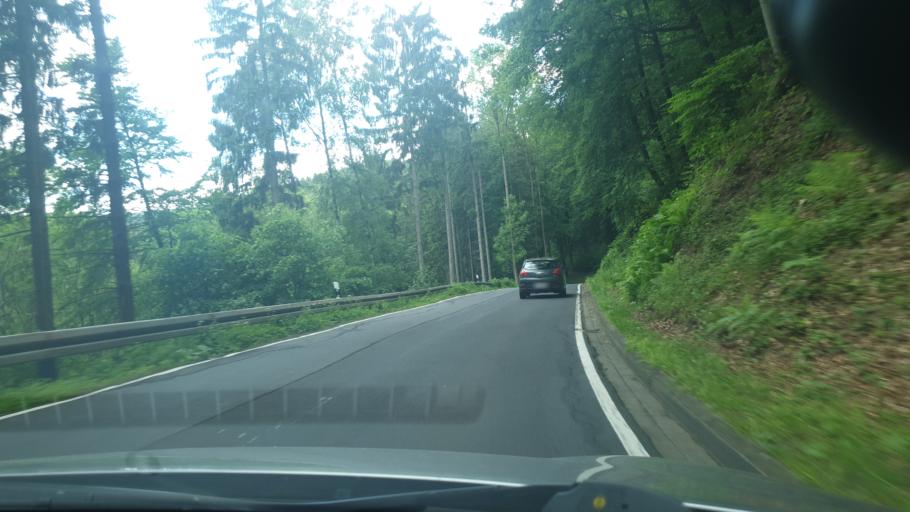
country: DE
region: Rheinland-Pfalz
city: Neuhausel
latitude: 50.3975
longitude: 7.7167
